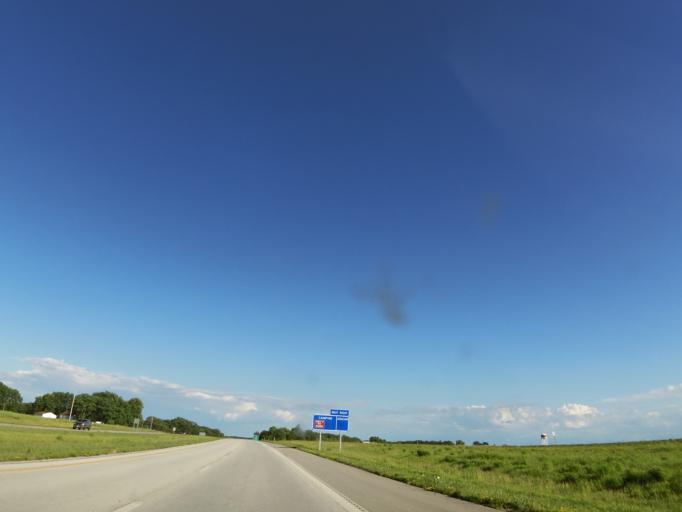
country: US
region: Missouri
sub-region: Pike County
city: Bowling Green
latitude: 39.3721
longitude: -91.2174
